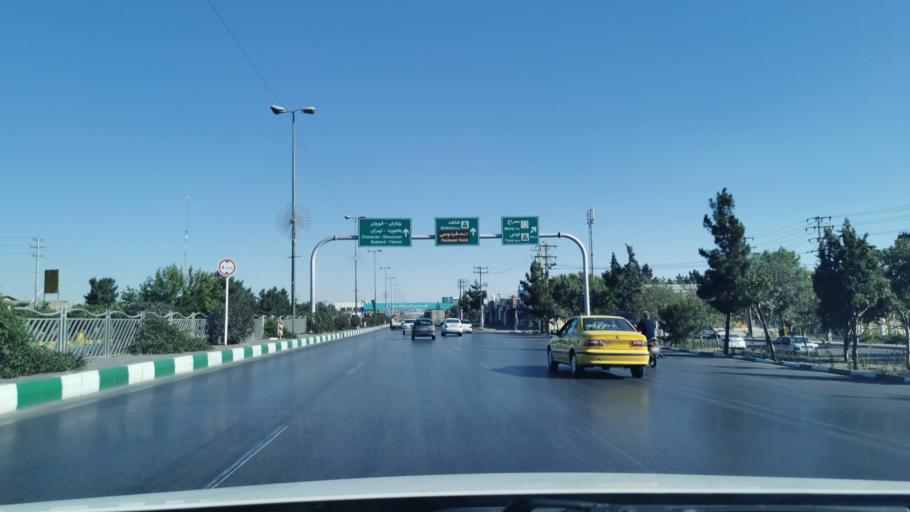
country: IR
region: Razavi Khorasan
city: Mashhad
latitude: 36.3509
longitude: 59.5453
